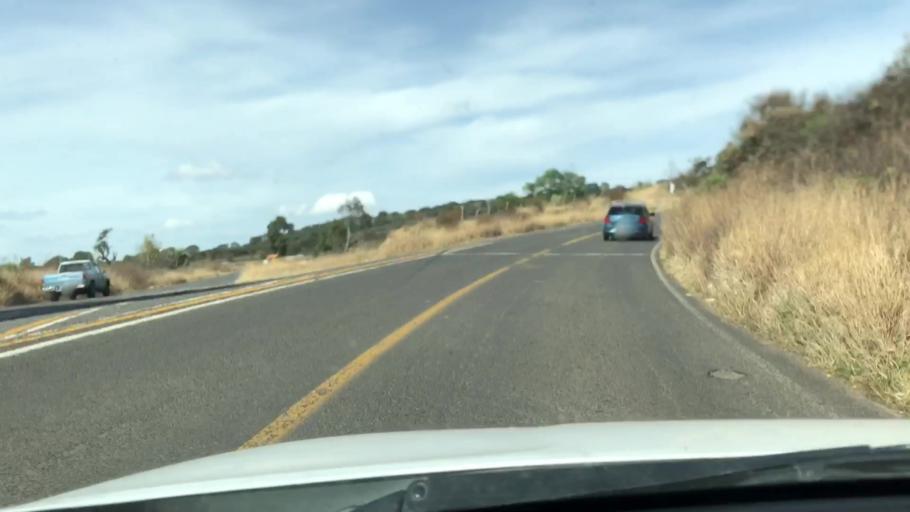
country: MX
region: Jalisco
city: Chiquilistlan
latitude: 20.1874
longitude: -103.7248
